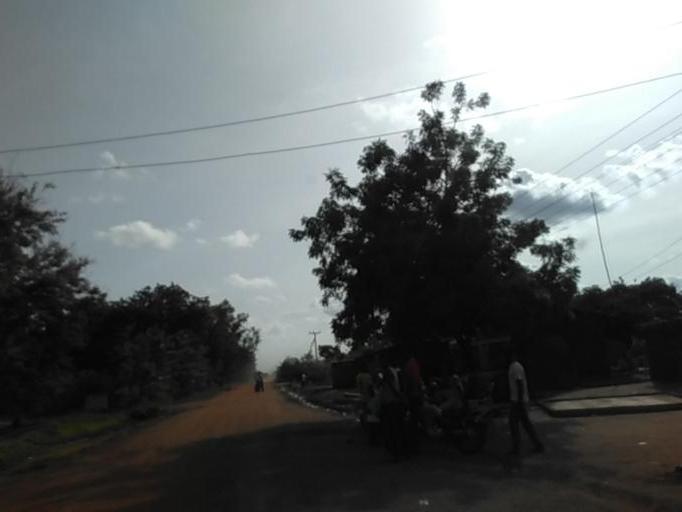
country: GH
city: Akropong
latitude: 6.0979
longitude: 0.2504
